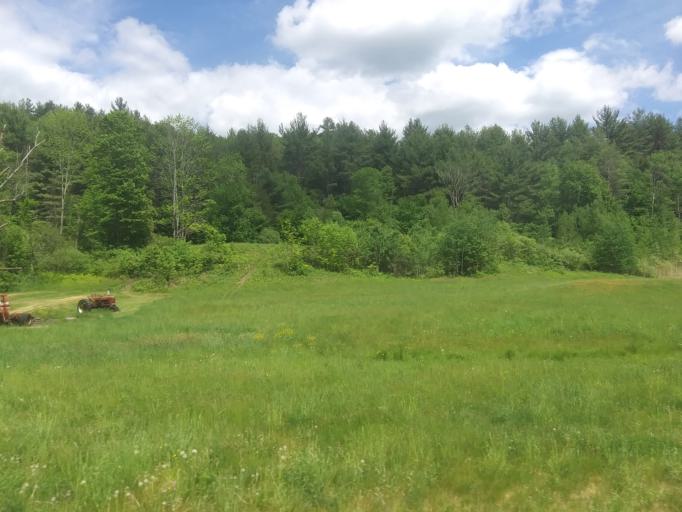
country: US
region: Massachusetts
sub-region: Franklin County
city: Buckland
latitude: 42.5738
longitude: -72.8110
